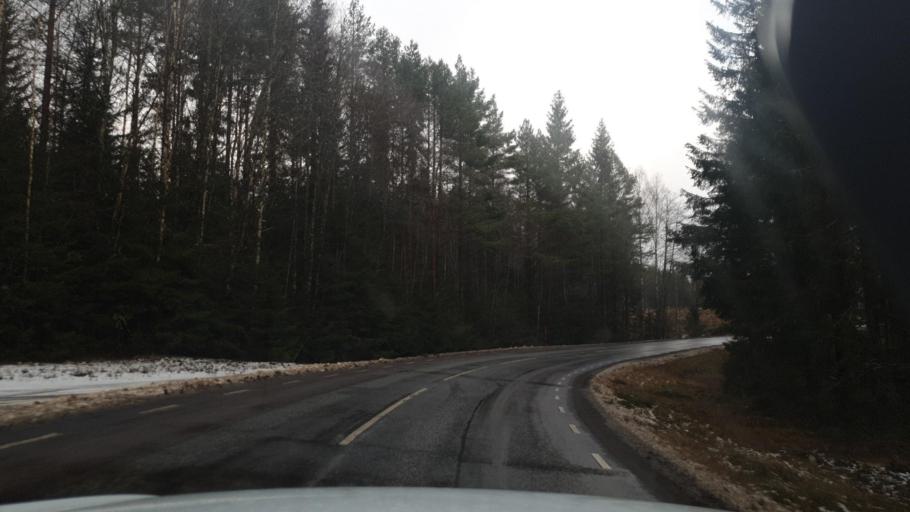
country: SE
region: Vaermland
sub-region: Eda Kommun
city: Amotfors
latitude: 59.6088
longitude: 12.3221
